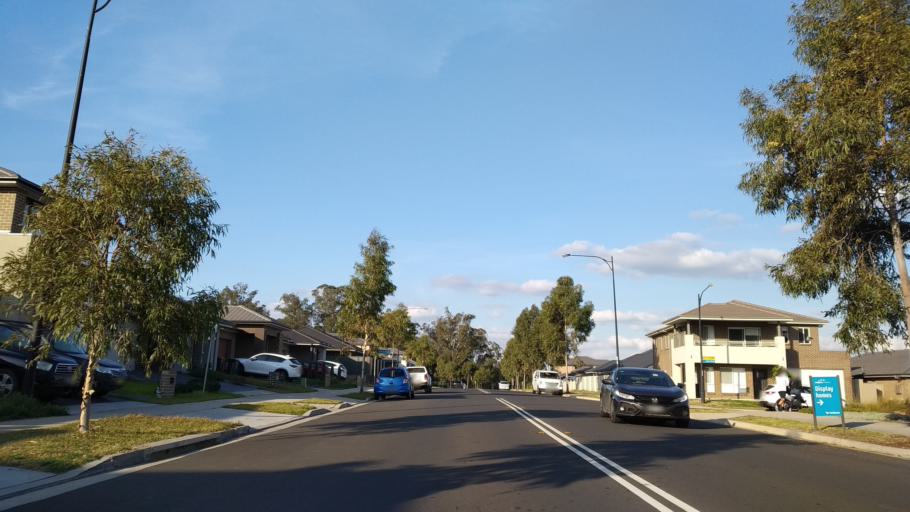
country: AU
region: New South Wales
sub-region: Penrith Municipality
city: Werrington Downs
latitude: -33.7227
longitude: 150.7307
